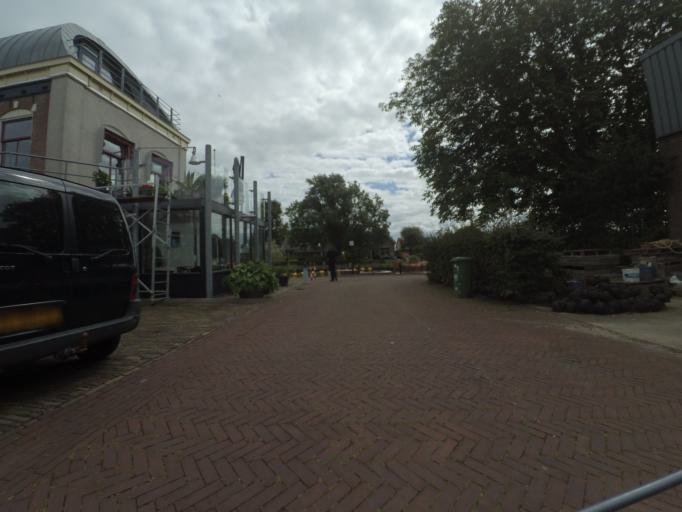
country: NL
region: Friesland
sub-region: Gemeente Kollumerland en Nieuwkruisland
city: Kollum
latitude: 53.3184
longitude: 6.1567
